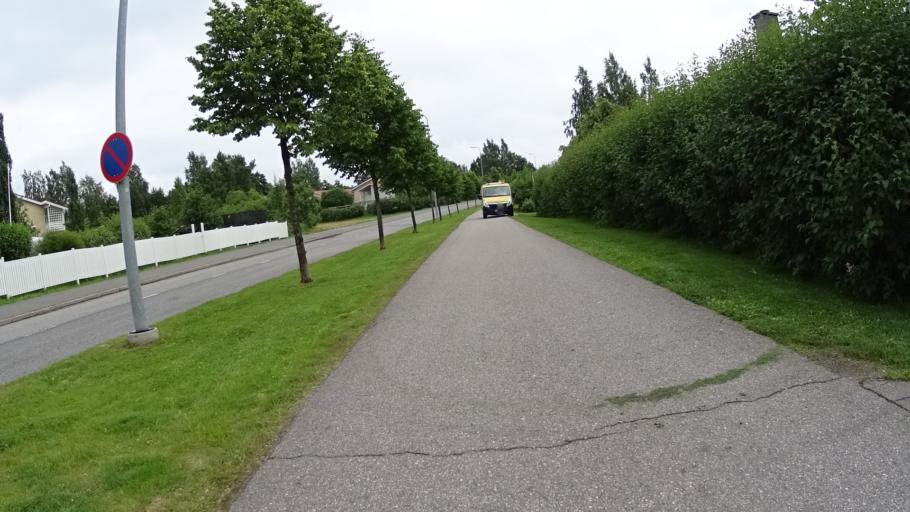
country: FI
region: Uusimaa
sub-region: Helsinki
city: Helsinki
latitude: 60.2773
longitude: 24.9118
